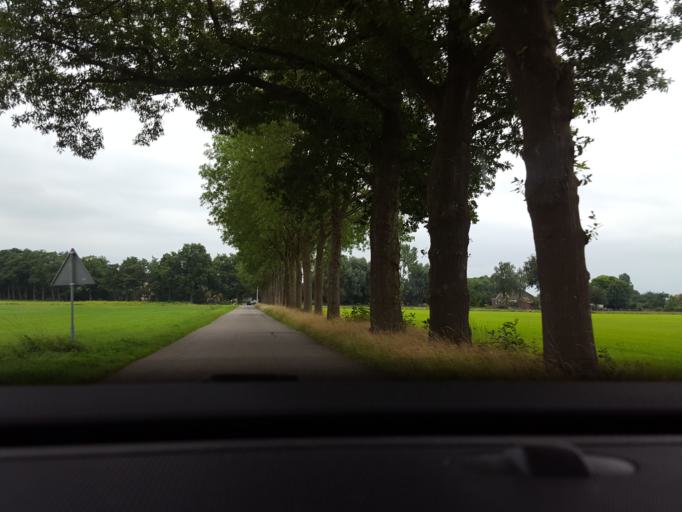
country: NL
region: Gelderland
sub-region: Gemeente Zutphen
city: Leesten
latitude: 52.1188
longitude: 6.2415
